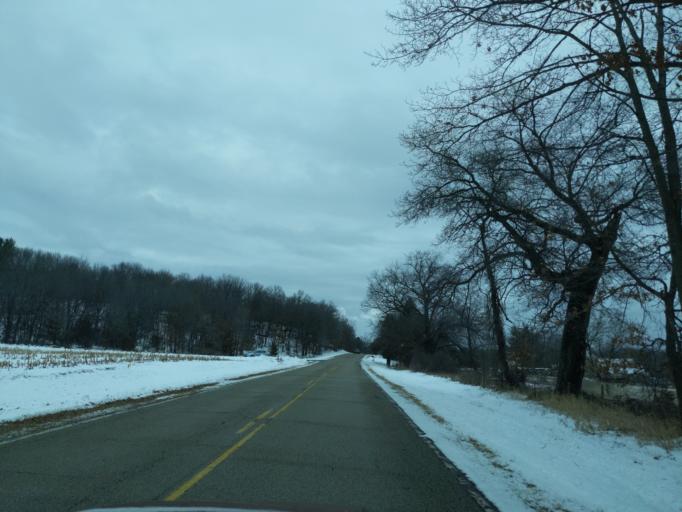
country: US
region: Wisconsin
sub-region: Marquette County
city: Montello
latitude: 43.9168
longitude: -89.3315
